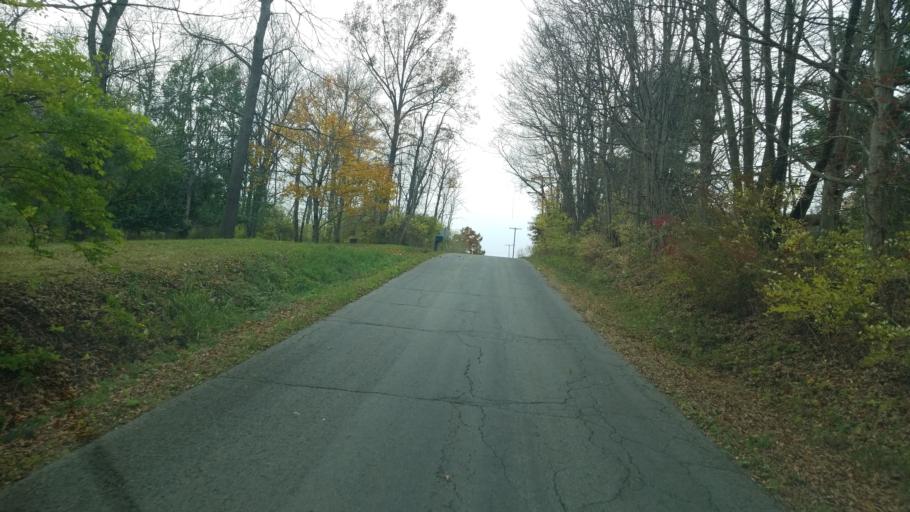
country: US
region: Ohio
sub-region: Richland County
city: Mansfield
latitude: 40.7261
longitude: -82.4911
